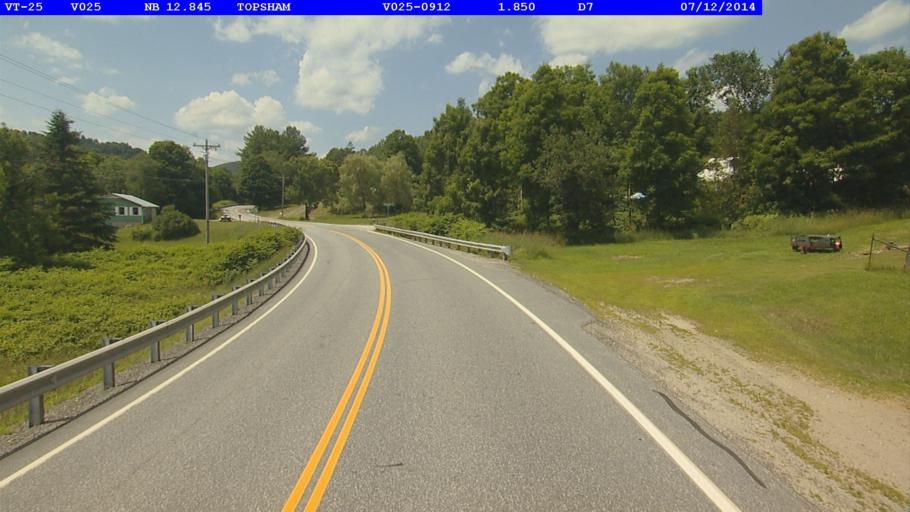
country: US
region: Vermont
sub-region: Orange County
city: Chelsea
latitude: 44.0944
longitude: -72.2897
